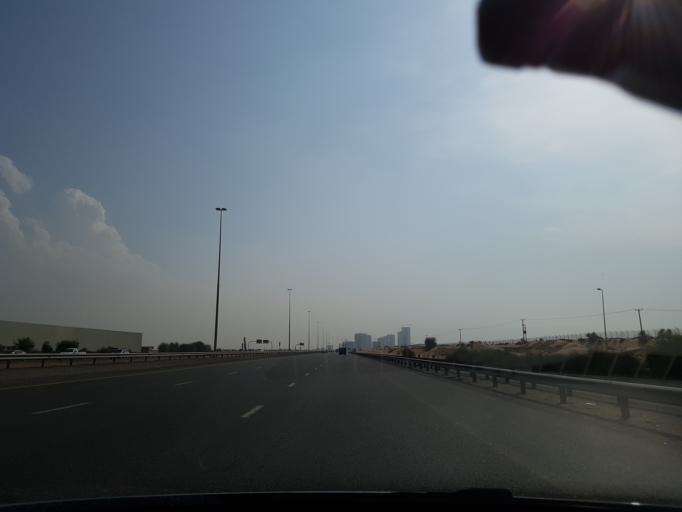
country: AE
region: Umm al Qaywayn
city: Umm al Qaywayn
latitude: 25.4215
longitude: 55.5906
